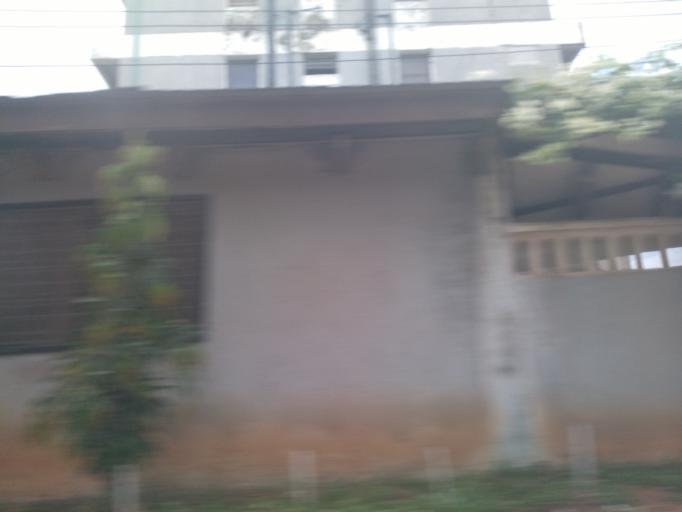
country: TZ
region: Dar es Salaam
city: Dar es Salaam
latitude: -6.7977
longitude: 39.2859
